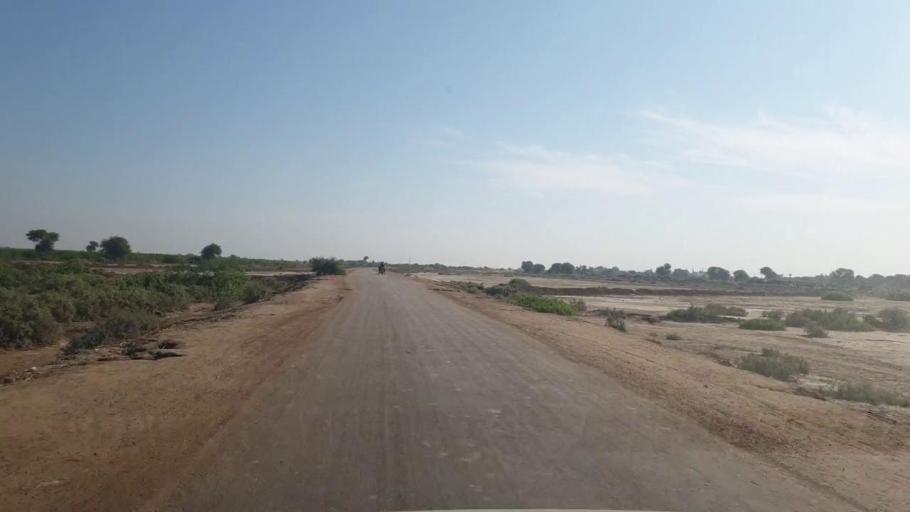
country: PK
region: Sindh
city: Rajo Khanani
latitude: 24.9238
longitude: 68.9373
